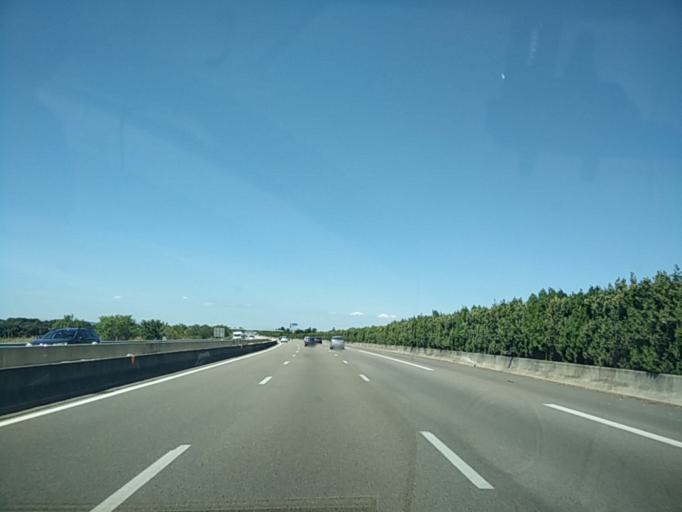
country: FR
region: Provence-Alpes-Cote d'Azur
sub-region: Departement du Vaucluse
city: Courthezon
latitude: 44.0969
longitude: 4.8702
